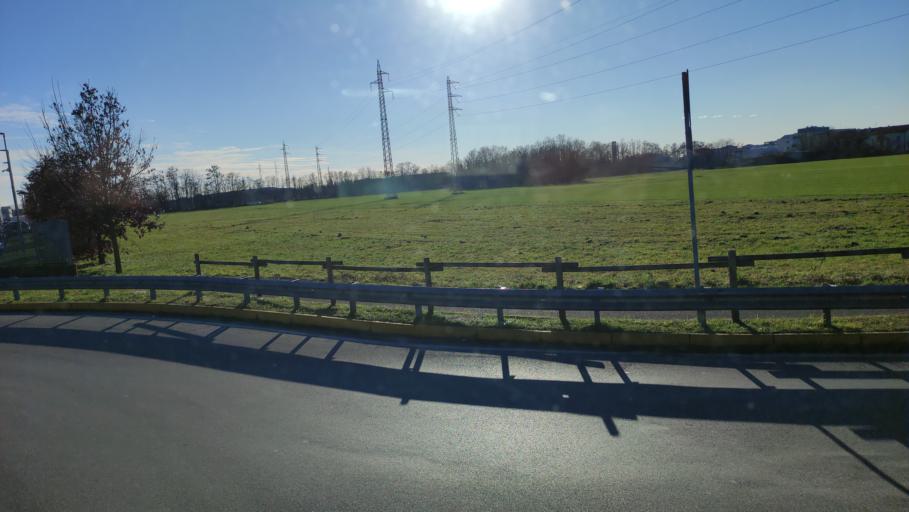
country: IT
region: Lombardy
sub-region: Provincia di Monza e Brianza
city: Concorezzo
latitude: 45.5913
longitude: 9.3211
